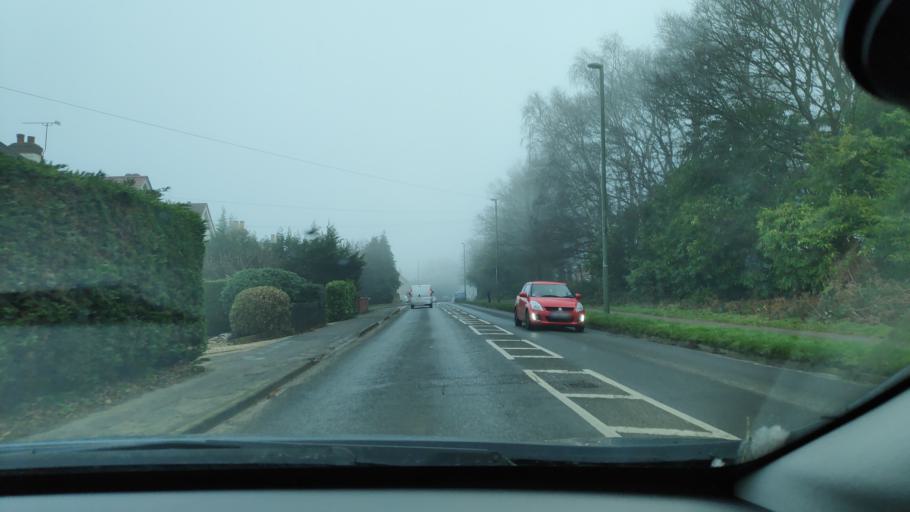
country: GB
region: England
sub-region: Surrey
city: Seale
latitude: 51.2623
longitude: -0.7221
